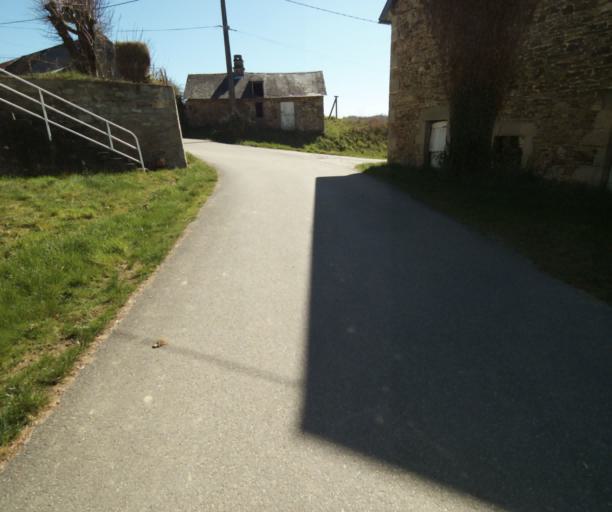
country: FR
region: Limousin
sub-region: Departement de la Correze
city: Chamboulive
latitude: 45.4560
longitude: 1.7043
